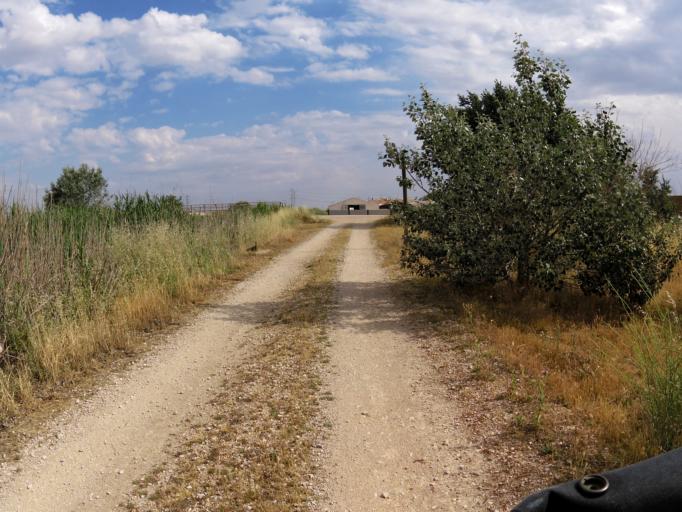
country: ES
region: Castille-La Mancha
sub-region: Provincia de Albacete
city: Albacete
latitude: 39.0282
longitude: -1.7917
